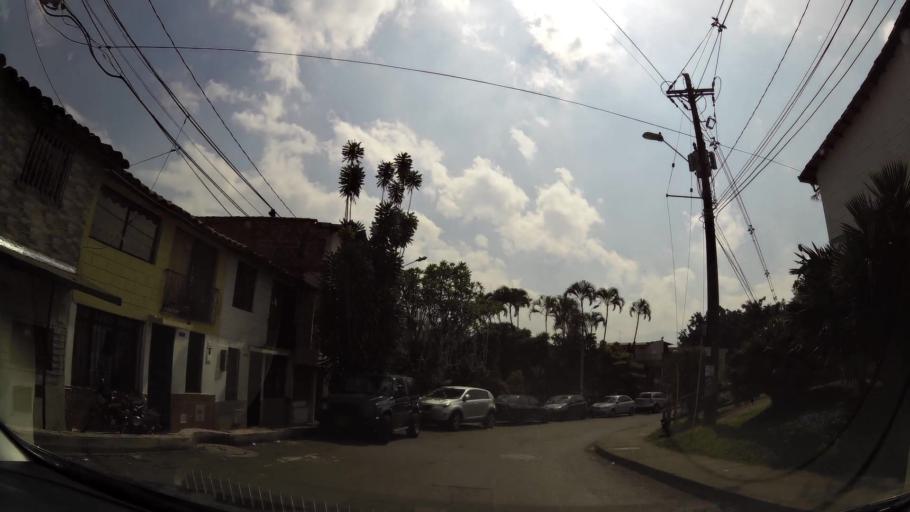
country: CO
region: Antioquia
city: La Estrella
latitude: 6.1774
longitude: -75.6385
